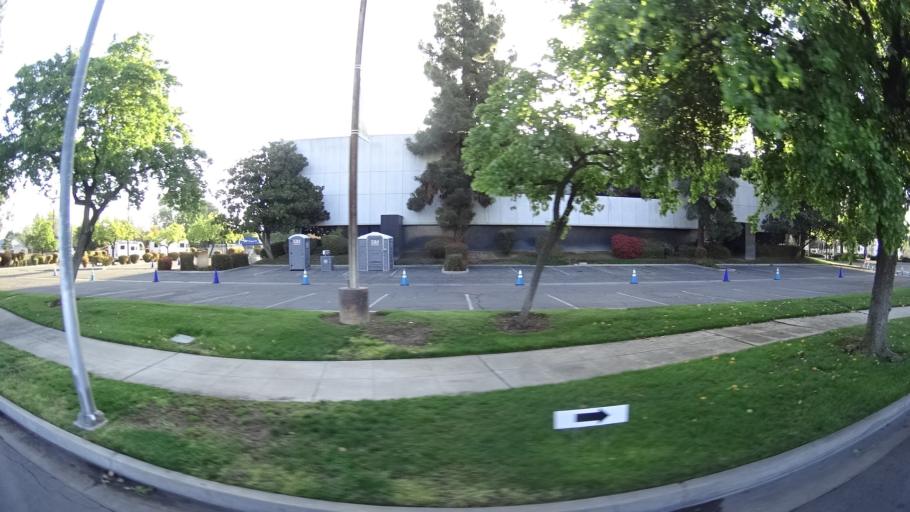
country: US
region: California
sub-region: Fresno County
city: Fresno
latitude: 36.8093
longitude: -119.7791
